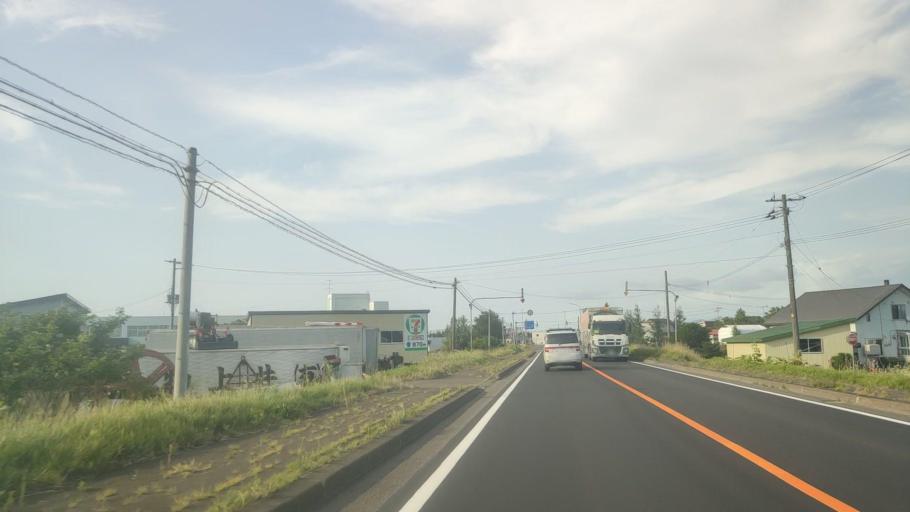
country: JP
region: Hokkaido
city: Iwamizawa
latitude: 43.0038
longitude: 141.7889
